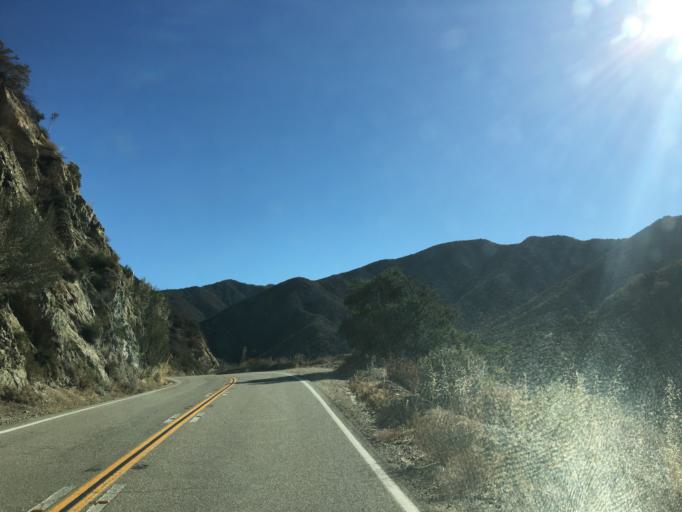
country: US
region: California
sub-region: Los Angeles County
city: Castaic
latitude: 34.6110
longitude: -118.5623
